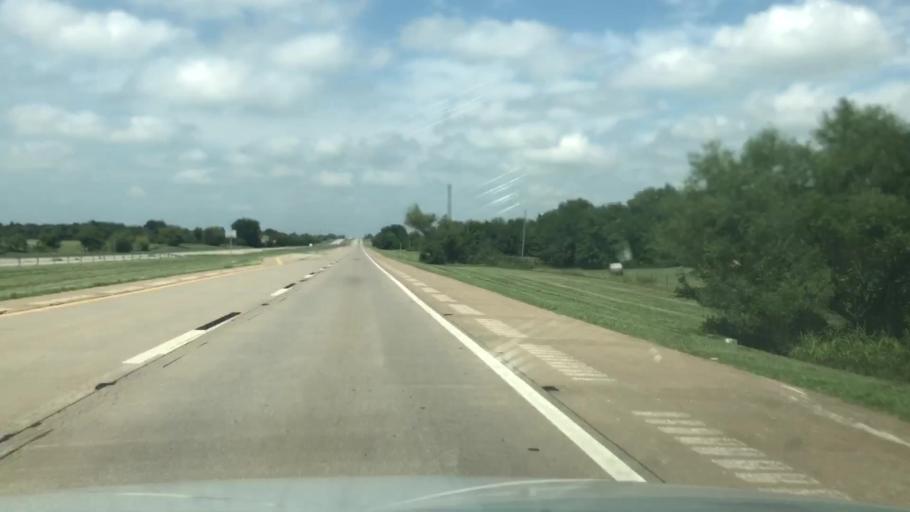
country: US
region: Oklahoma
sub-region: Osage County
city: Skiatook
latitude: 36.3934
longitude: -95.9203
